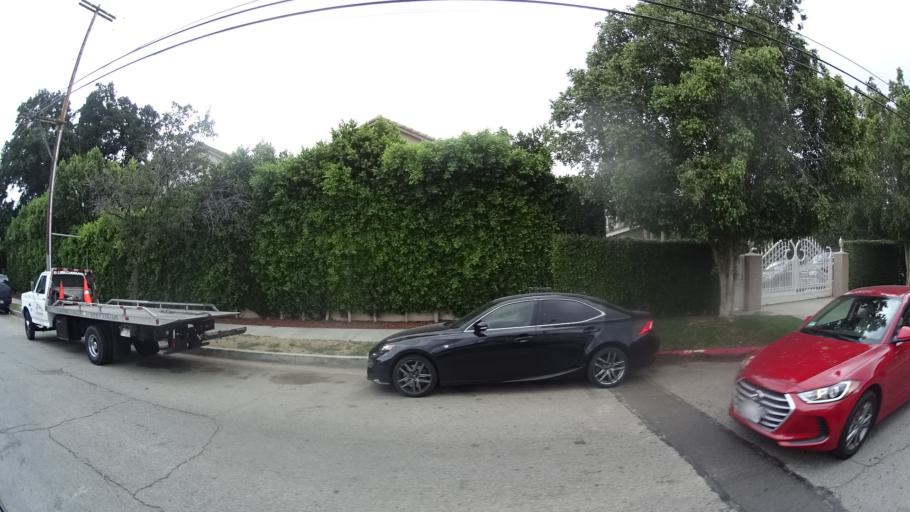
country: US
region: California
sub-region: Los Angeles County
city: San Fernando
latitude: 34.2404
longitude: -118.4632
